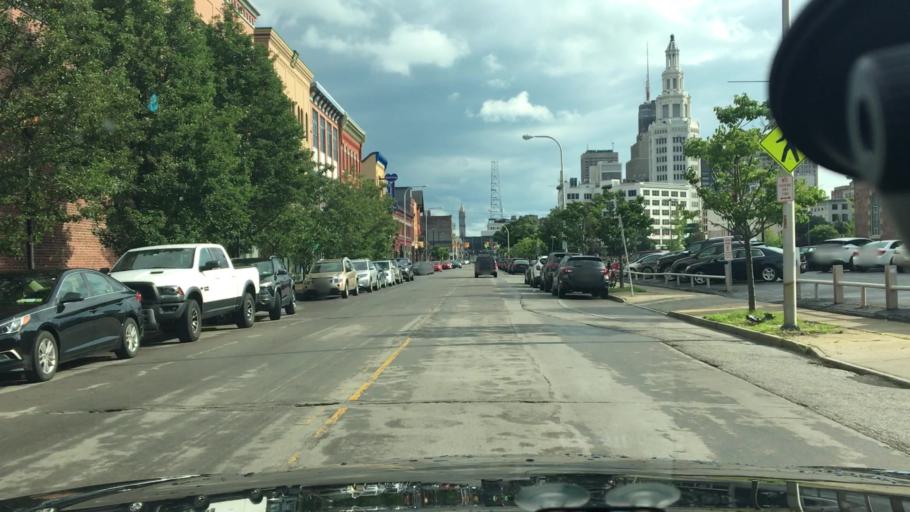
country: US
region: New York
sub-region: Erie County
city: Buffalo
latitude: 42.8916
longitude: -78.8702
